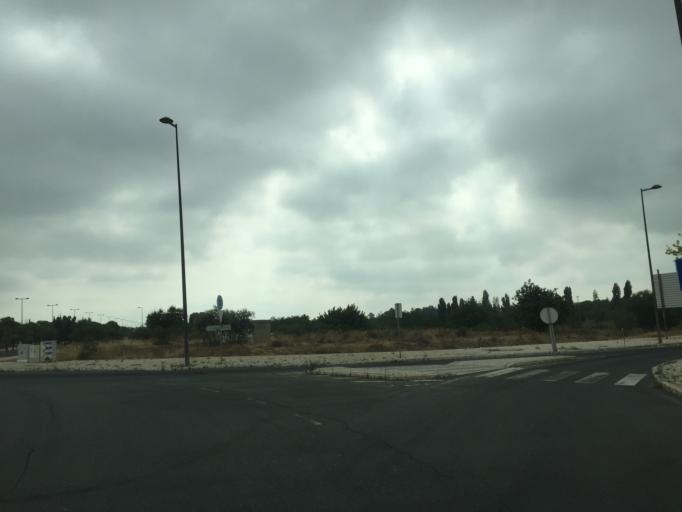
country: PT
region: Faro
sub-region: Faro
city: Santa Barbara de Nexe
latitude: 37.0863
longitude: -7.9791
